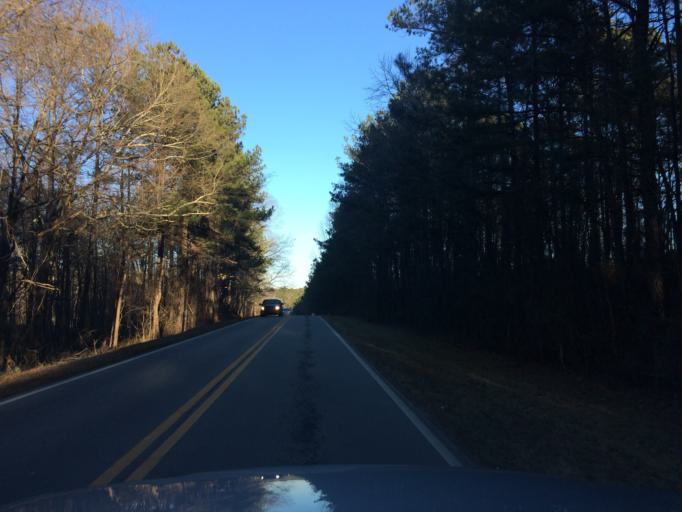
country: US
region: Georgia
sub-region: Barrow County
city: Winder
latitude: 33.9703
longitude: -83.7780
